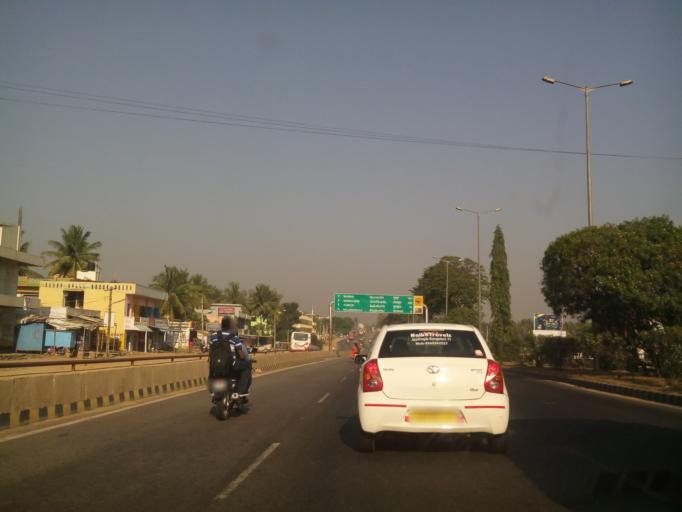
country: IN
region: Karnataka
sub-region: Bangalore Rural
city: Nelamangala
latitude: 13.0776
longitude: 77.4309
